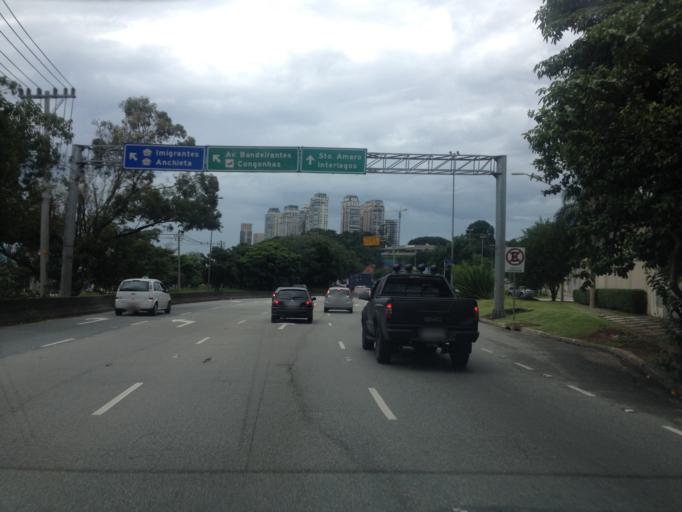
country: BR
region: Sao Paulo
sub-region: Sao Paulo
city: Sao Paulo
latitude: -23.5899
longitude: -46.6934
